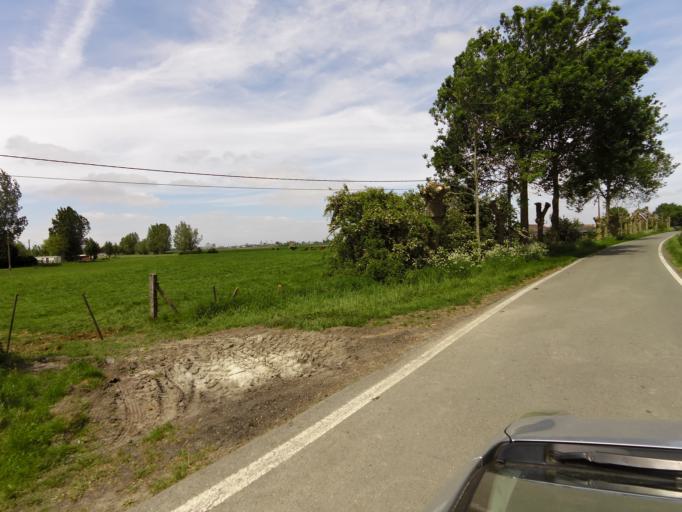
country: BE
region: Flanders
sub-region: Provincie West-Vlaanderen
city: Diksmuide
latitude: 51.0214
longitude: 2.8486
